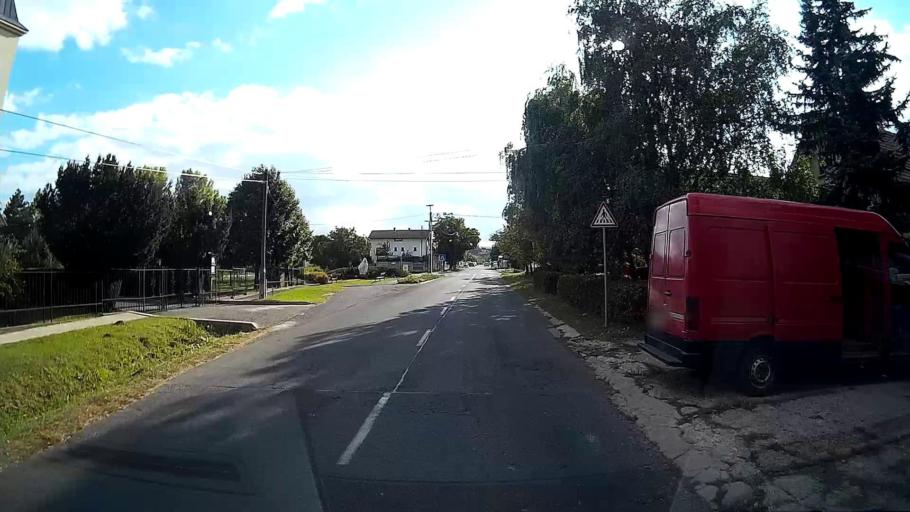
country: HU
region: Pest
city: Pilisvorosvar
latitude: 47.6321
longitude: 18.8989
